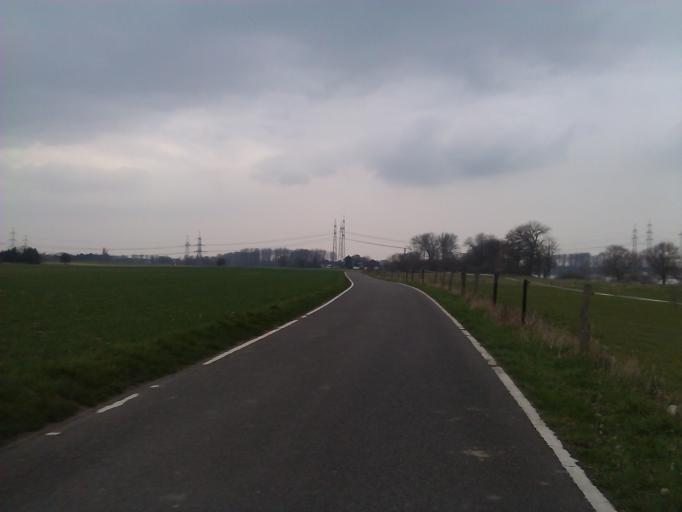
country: DE
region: North Rhine-Westphalia
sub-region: Regierungsbezirk Koln
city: Leverkusen
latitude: 51.0339
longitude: 6.9532
